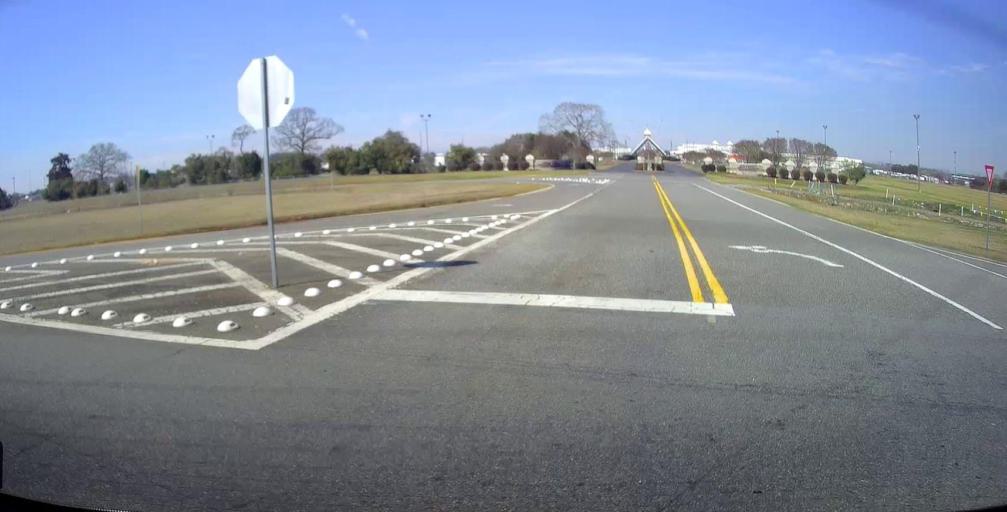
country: US
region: Georgia
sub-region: Houston County
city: Perry
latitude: 32.4307
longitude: -83.7500
